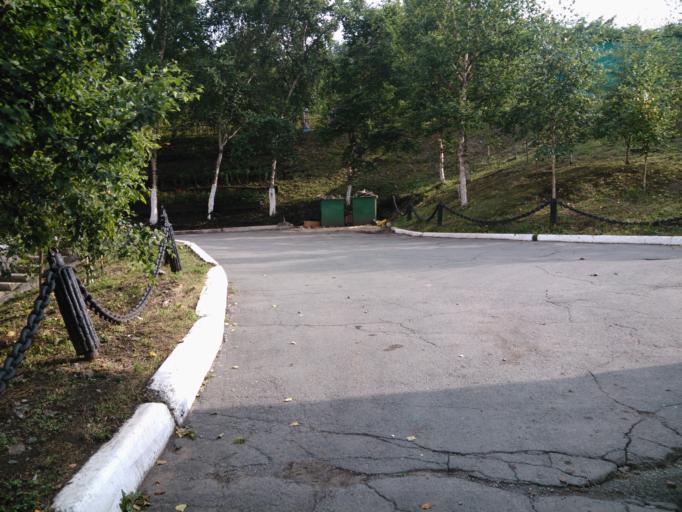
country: RU
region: Primorskiy
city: Vladivostok
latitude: 43.0946
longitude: 131.9604
